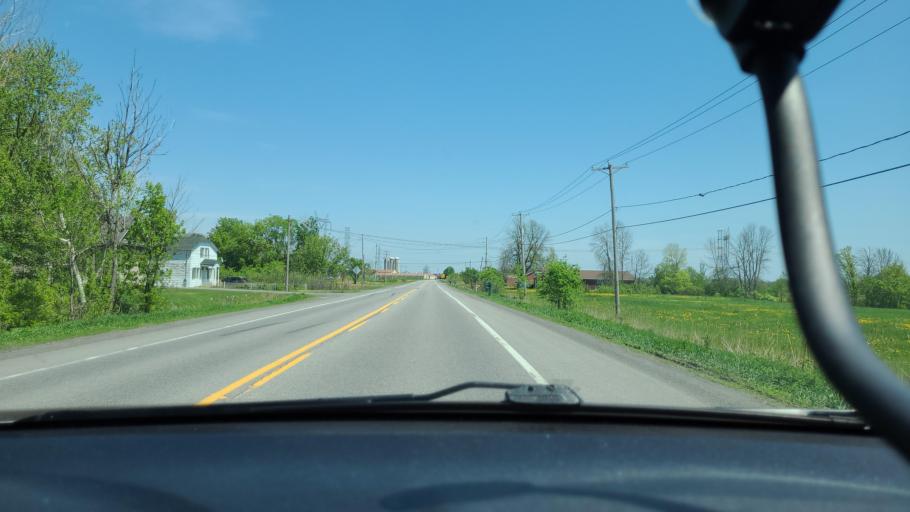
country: CA
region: Quebec
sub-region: Laurentides
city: Mirabel
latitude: 45.6016
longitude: -74.0527
